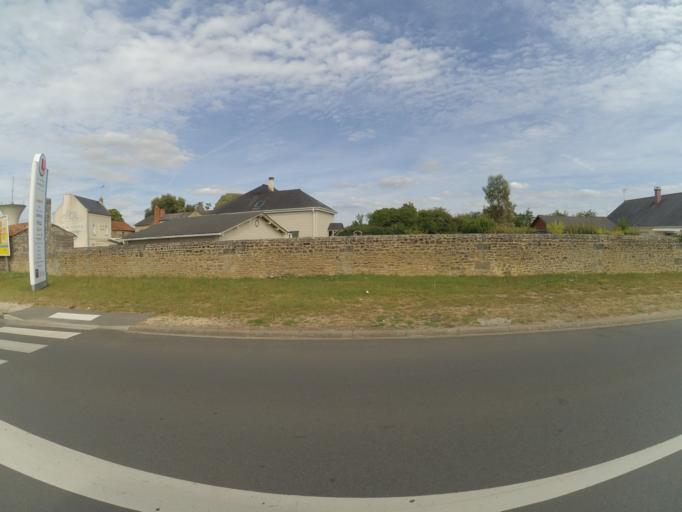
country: FR
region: Pays de la Loire
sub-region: Departement de Maine-et-Loire
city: Doue-la-Fontaine
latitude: 47.1925
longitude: -0.2894
